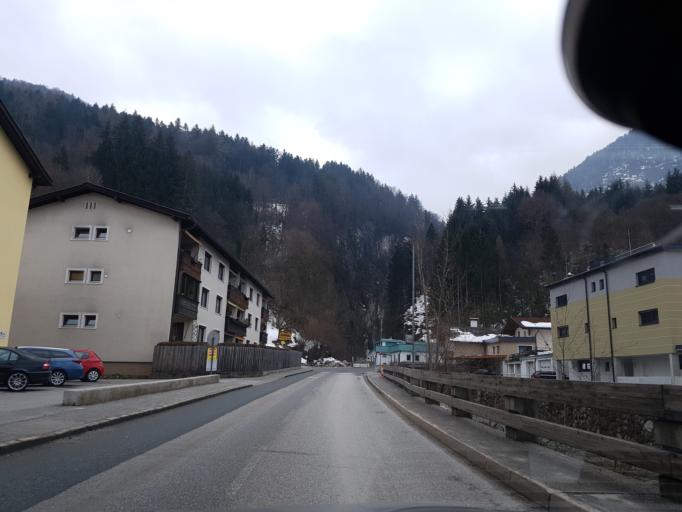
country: AT
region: Tyrol
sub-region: Politischer Bezirk Kufstein
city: Worgl
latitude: 47.4807
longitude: 12.0712
